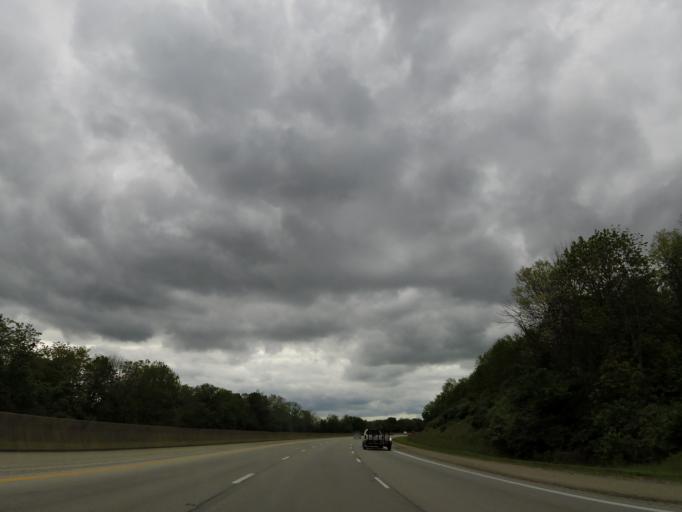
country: US
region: Kentucky
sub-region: Boone County
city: Walton
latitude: 38.8422
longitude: -84.6179
